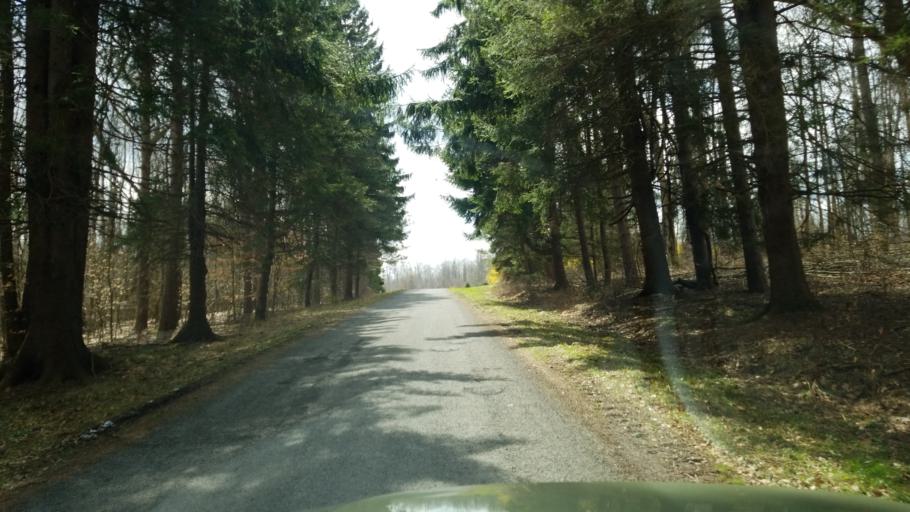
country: US
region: Pennsylvania
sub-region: Jefferson County
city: Brockway
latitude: 41.2812
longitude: -78.8699
